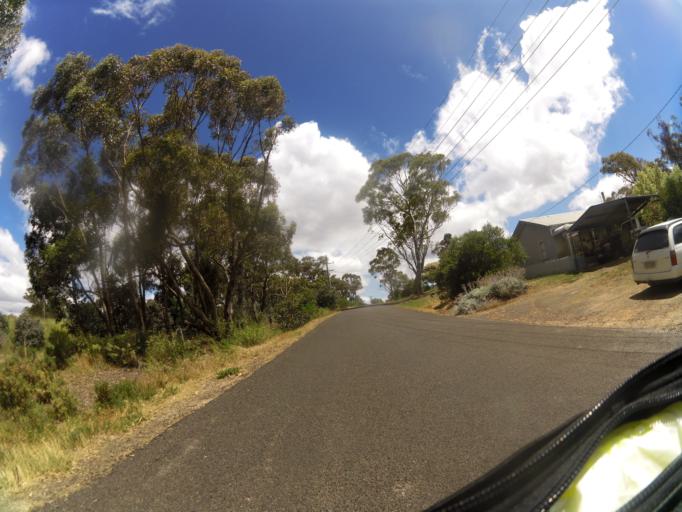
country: AU
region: Victoria
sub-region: Mount Alexander
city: Castlemaine
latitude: -37.0027
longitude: 144.2535
